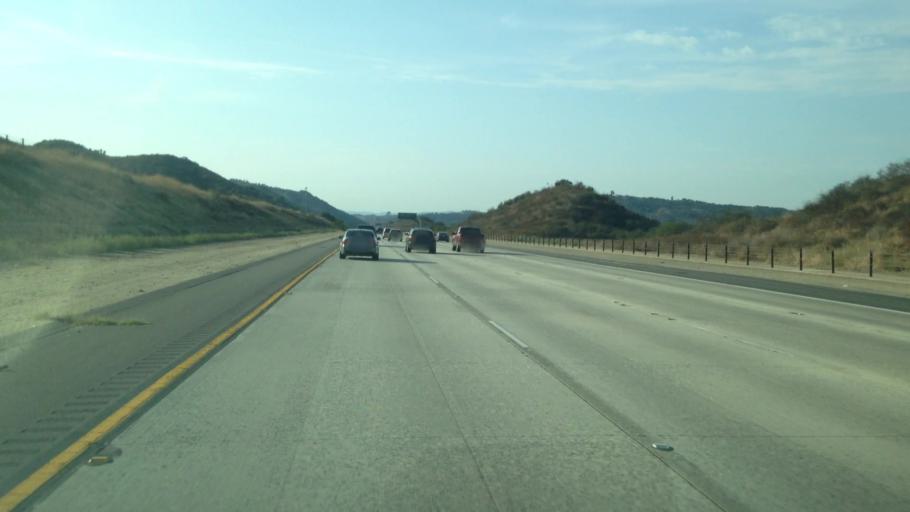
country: US
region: California
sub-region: San Diego County
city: Hidden Meadows
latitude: 33.2294
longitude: -117.1456
